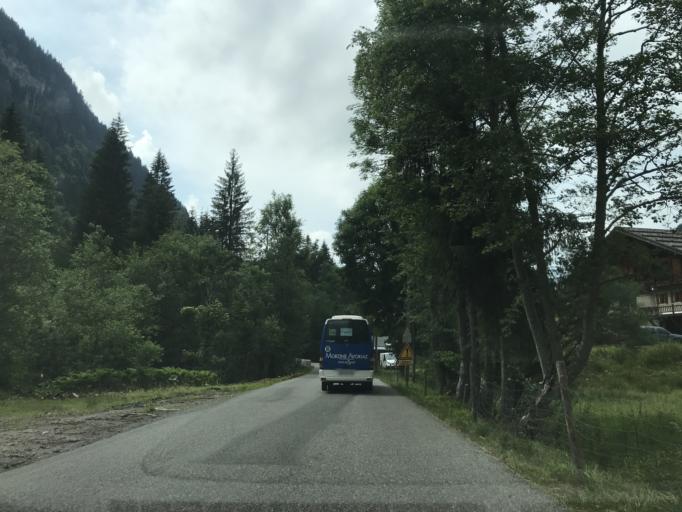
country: FR
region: Rhone-Alpes
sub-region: Departement de la Haute-Savoie
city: Morzine
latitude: 46.1581
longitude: 6.7304
